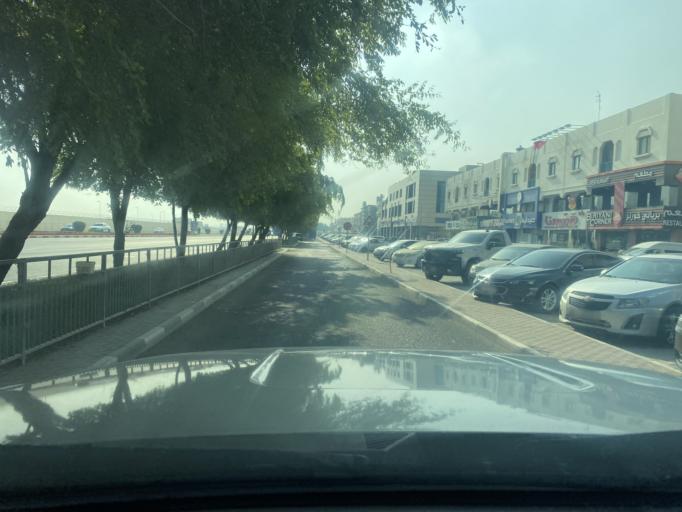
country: QA
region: Baladiyat ad Dawhah
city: Doha
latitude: 25.2434
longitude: 51.5692
